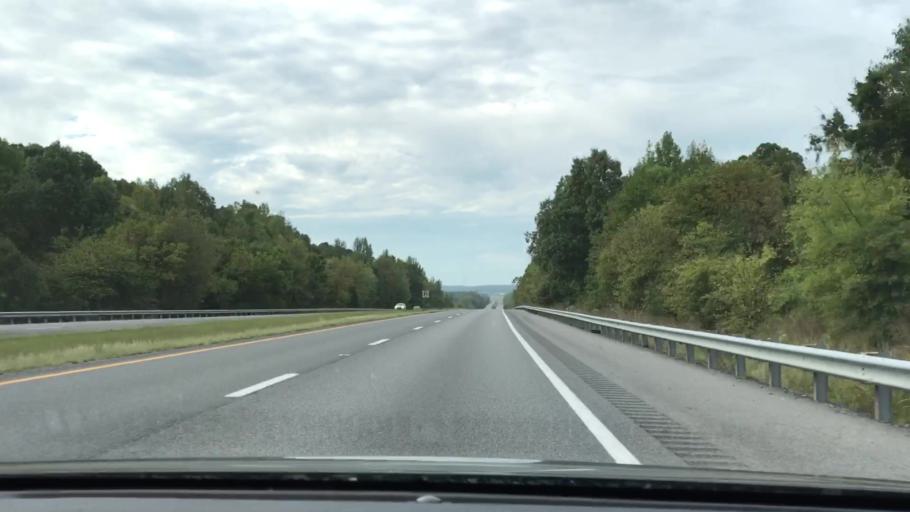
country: US
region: Kentucky
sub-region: Marshall County
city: Benton
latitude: 36.8944
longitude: -88.3494
